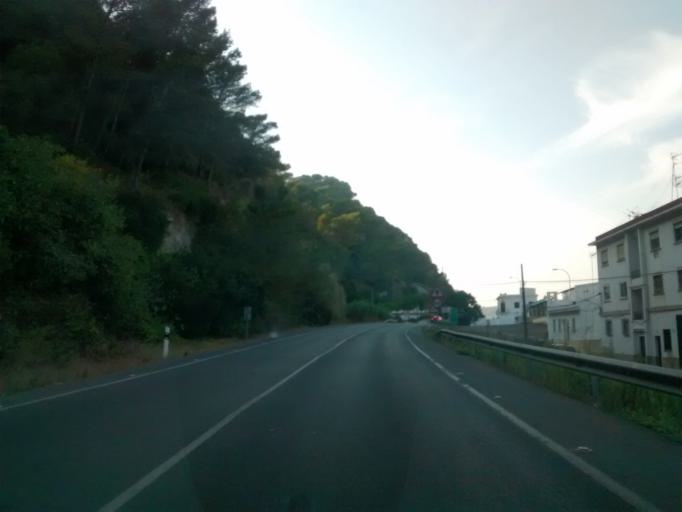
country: ES
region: Andalusia
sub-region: Provincia de Cadiz
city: Vejer de la Frontera
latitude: 36.2513
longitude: -5.9552
